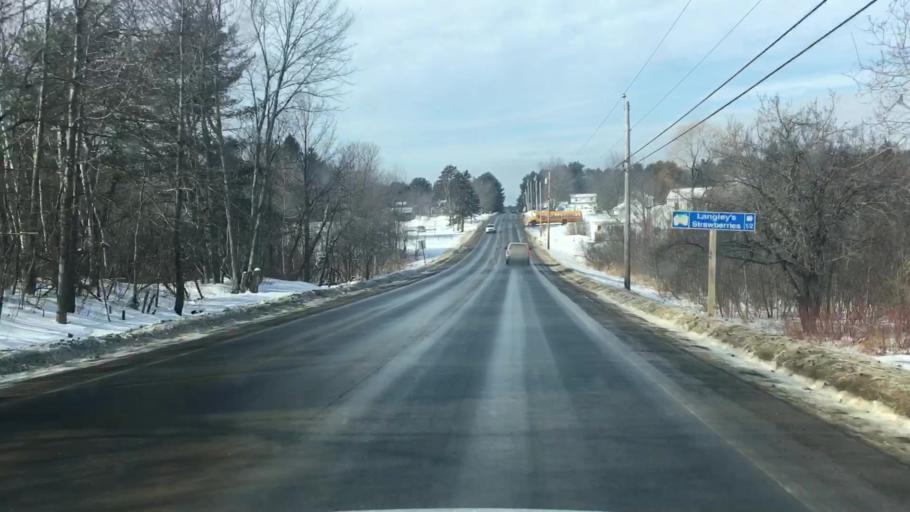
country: US
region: Maine
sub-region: Penobscot County
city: Hermon
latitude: 44.8500
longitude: -68.8786
